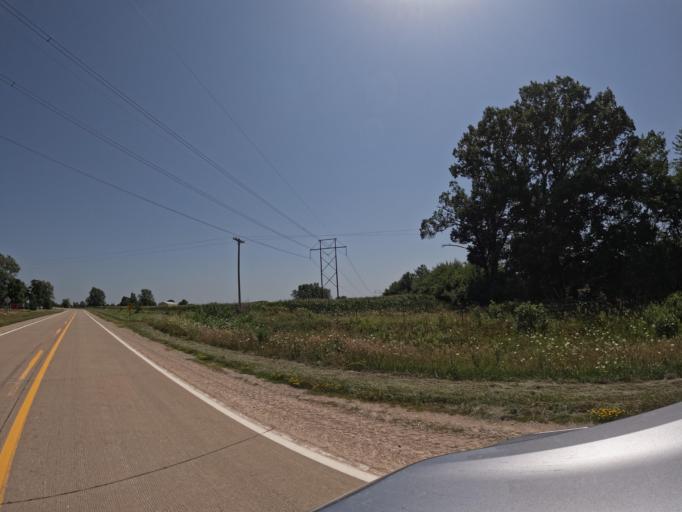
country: US
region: Iowa
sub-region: Henry County
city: Mount Pleasant
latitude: 40.9839
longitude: -91.6312
